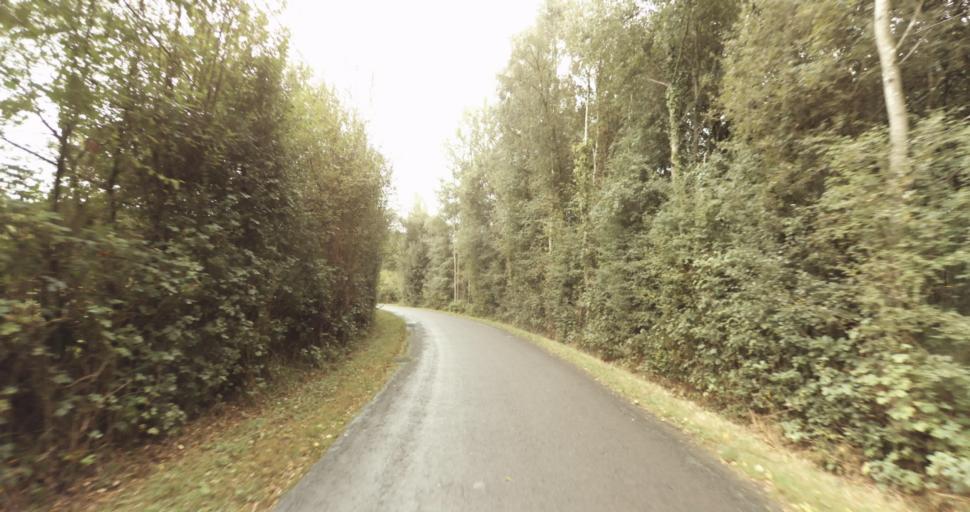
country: FR
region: Lower Normandy
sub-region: Departement de l'Orne
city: Sainte-Gauburge-Sainte-Colombe
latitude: 48.6984
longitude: 0.4538
